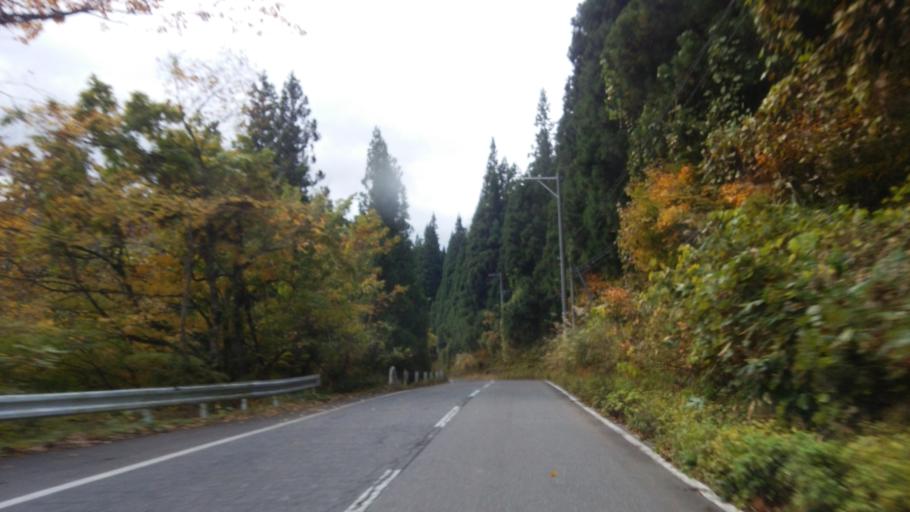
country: JP
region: Fukushima
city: Kitakata
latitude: 37.4125
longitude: 139.6998
